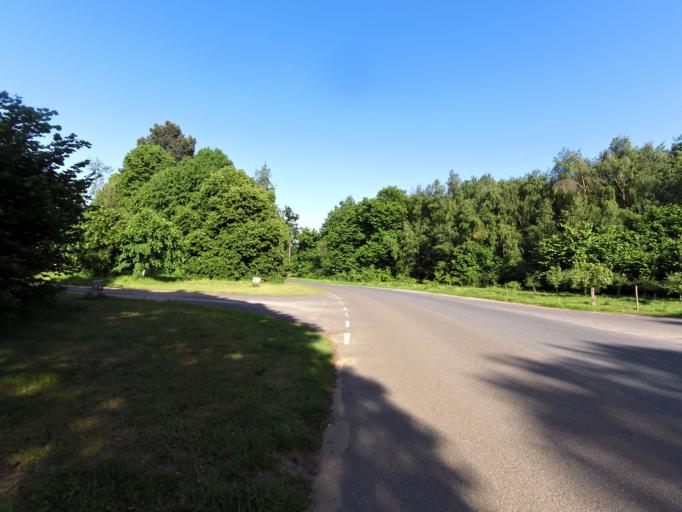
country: GB
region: England
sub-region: Suffolk
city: Woodbridge
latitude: 52.0956
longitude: 1.3485
